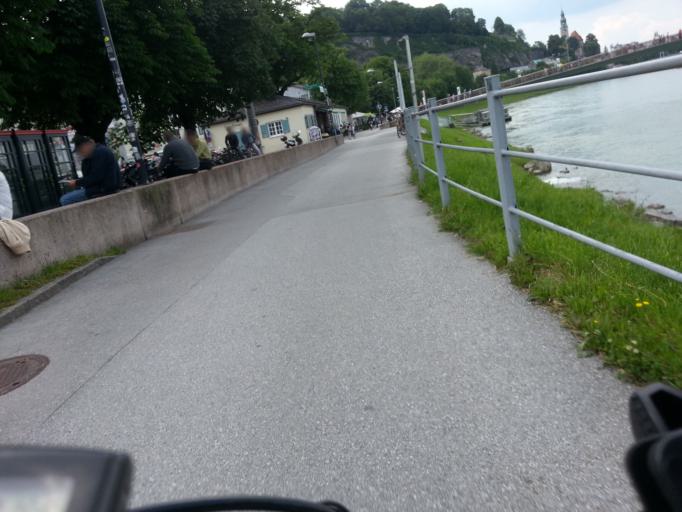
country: AT
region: Salzburg
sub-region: Salzburg Stadt
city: Salzburg
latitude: 47.8008
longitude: 13.0433
